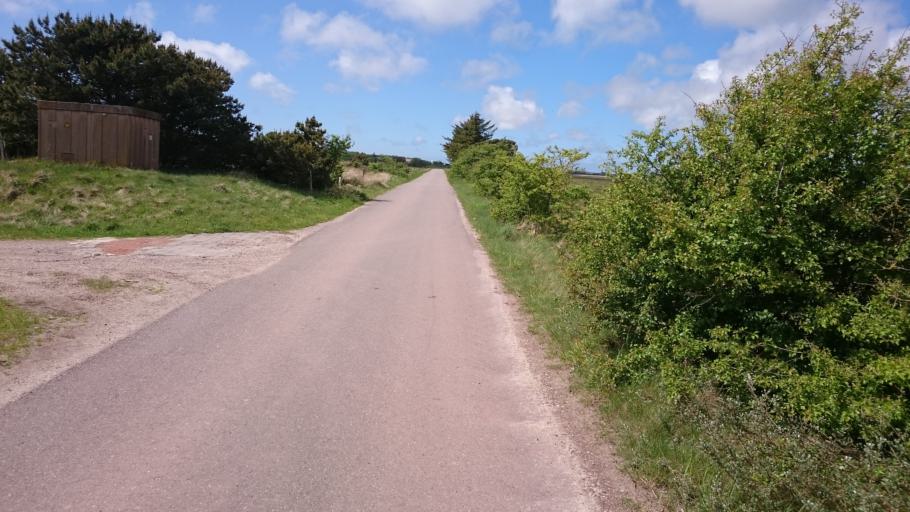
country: DK
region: South Denmark
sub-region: Fano Kommune
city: Nordby
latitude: 55.4216
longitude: 8.4223
